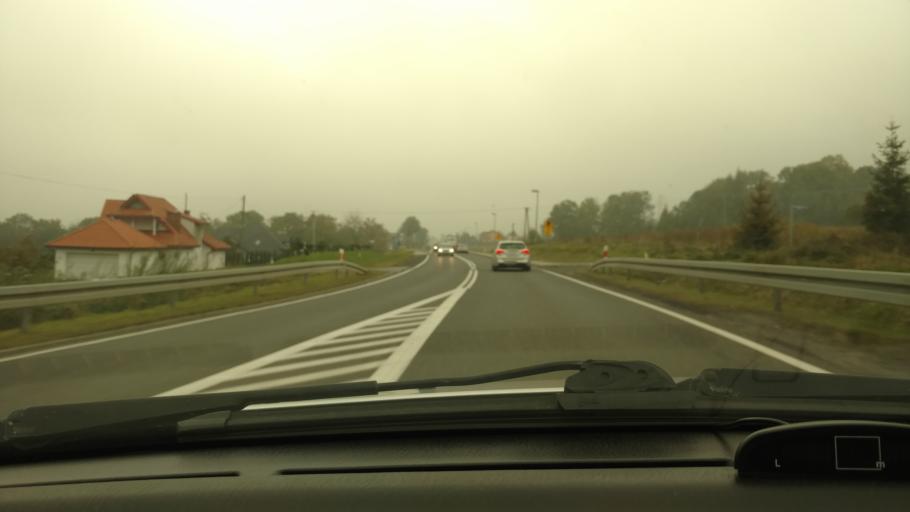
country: PL
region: Lesser Poland Voivodeship
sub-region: Powiat nowosadecki
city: Kamionka Wielka
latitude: 49.6170
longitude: 20.8659
